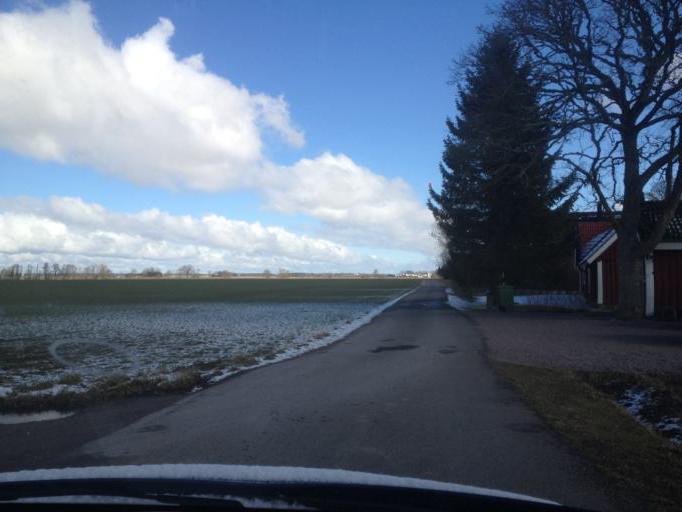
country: SE
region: OEstergoetland
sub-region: Mjolby Kommun
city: Mantorp
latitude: 58.4455
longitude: 15.3284
